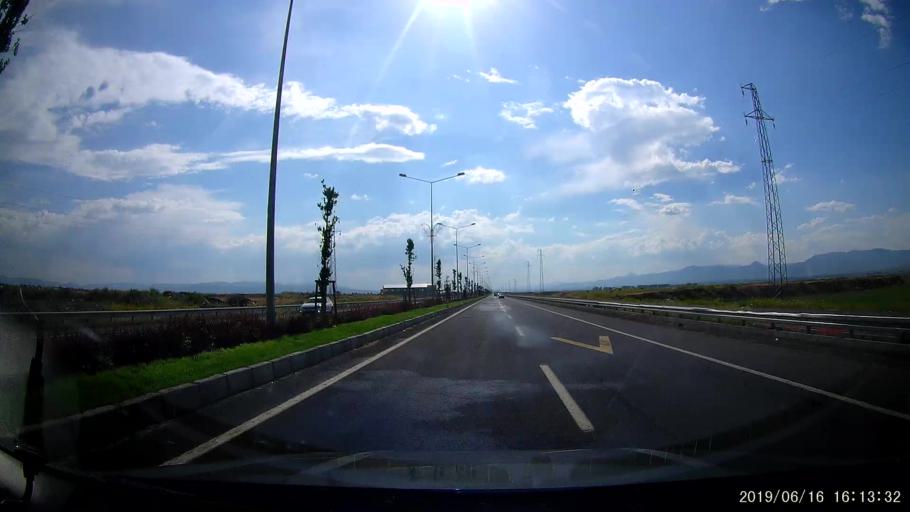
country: TR
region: Erzurum
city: Erzurum
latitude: 39.9597
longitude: 41.2701
